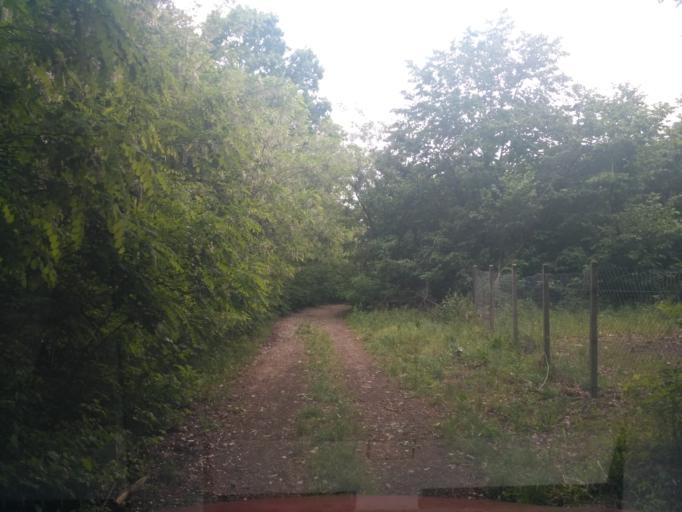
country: SK
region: Kosicky
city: Moldava nad Bodvou
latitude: 48.6942
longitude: 21.0766
